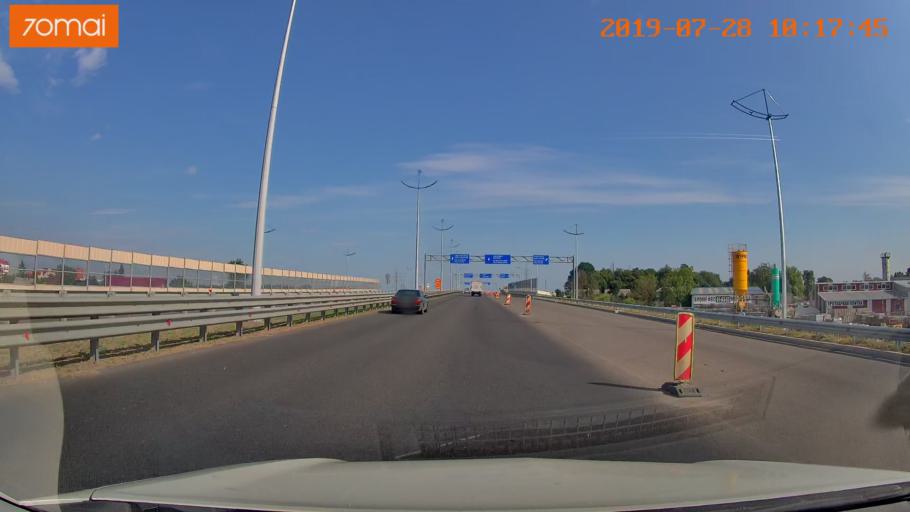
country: RU
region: Kaliningrad
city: Maloye Isakovo
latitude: 54.7438
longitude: 20.5926
